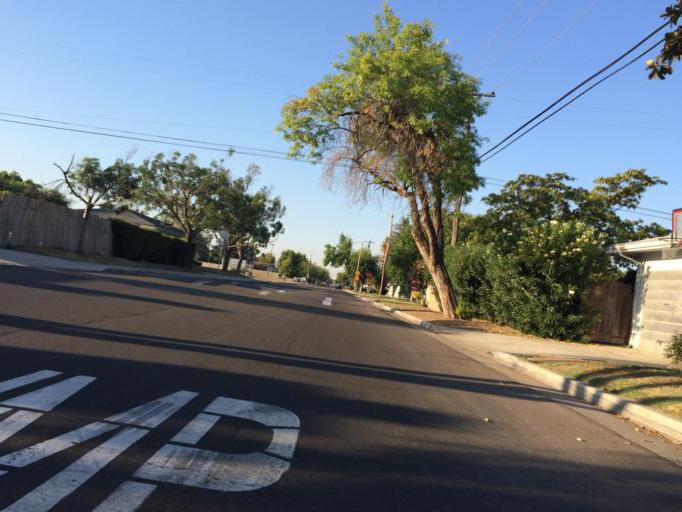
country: US
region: California
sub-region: Fresno County
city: Fresno
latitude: 36.7712
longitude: -119.7409
